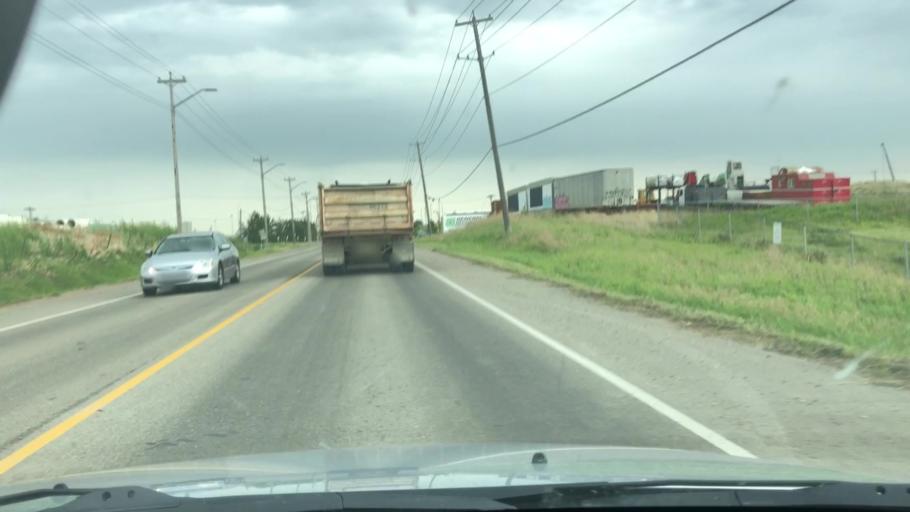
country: CA
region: Alberta
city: Sherwood Park
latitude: 53.5211
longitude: -113.3940
